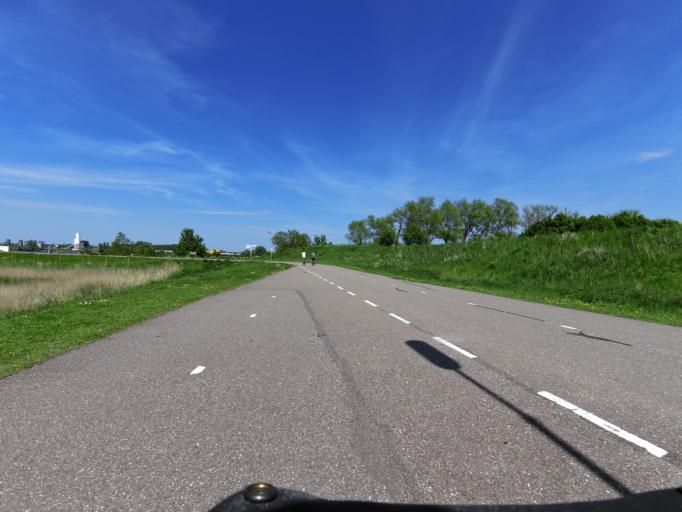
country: NL
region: South Holland
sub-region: Gemeente Binnenmaas
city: Heinenoord
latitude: 51.8293
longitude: 4.5112
